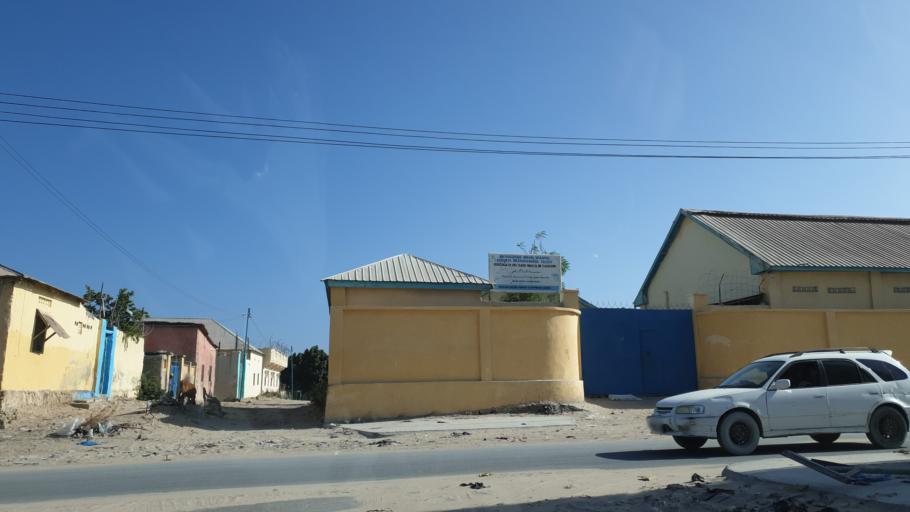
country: SO
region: Banaadir
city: Mogadishu
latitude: 2.0517
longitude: 45.3104
